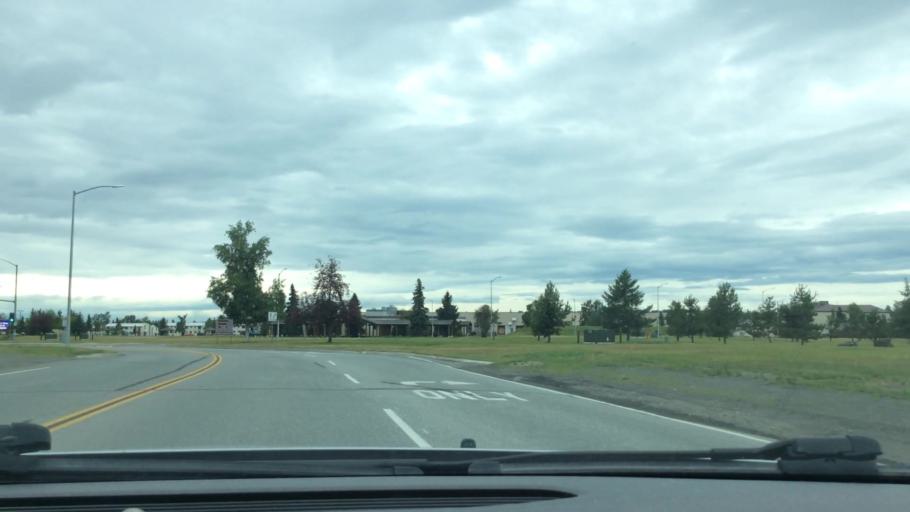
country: US
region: Alaska
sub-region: Anchorage Municipality
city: Anchorage
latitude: 61.2396
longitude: -149.7985
